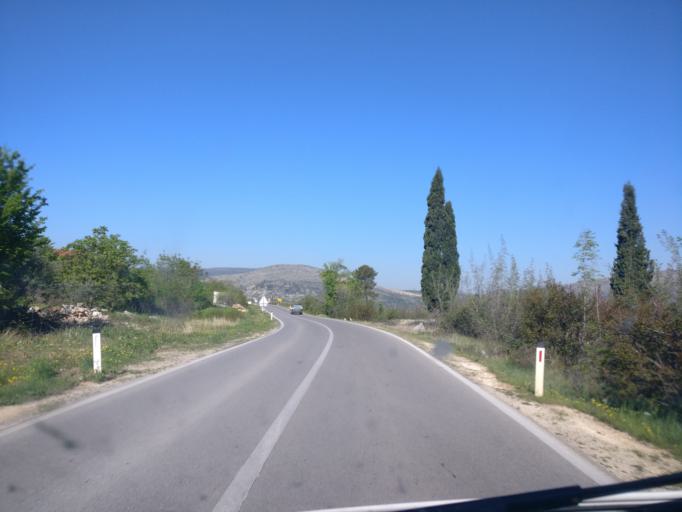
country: BA
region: Federation of Bosnia and Herzegovina
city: Tasovcici
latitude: 43.1196
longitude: 17.7339
